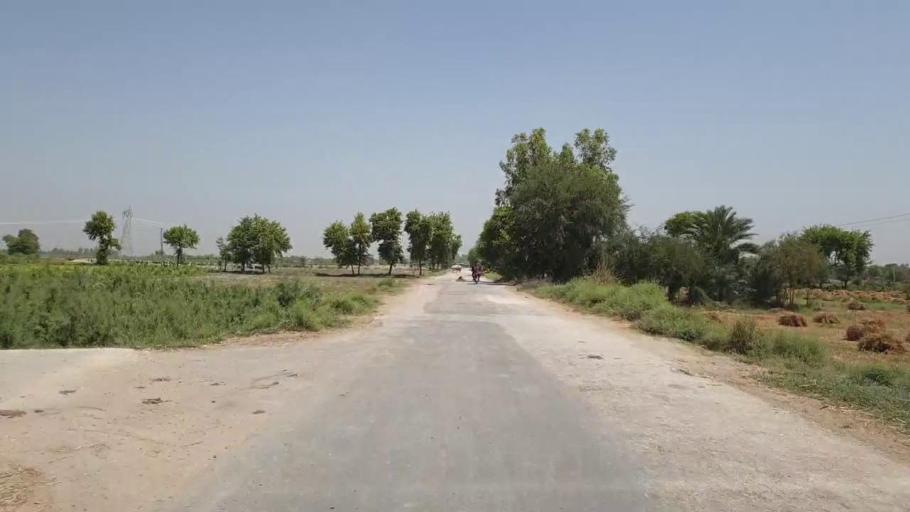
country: PK
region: Sindh
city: Adilpur
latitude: 27.8877
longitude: 69.2884
